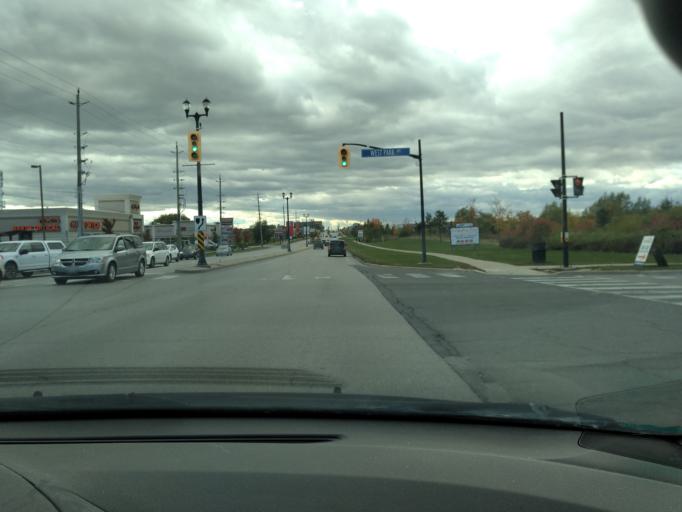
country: CA
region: Ontario
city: Bradford West Gwillimbury
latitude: 44.1099
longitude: -79.5845
